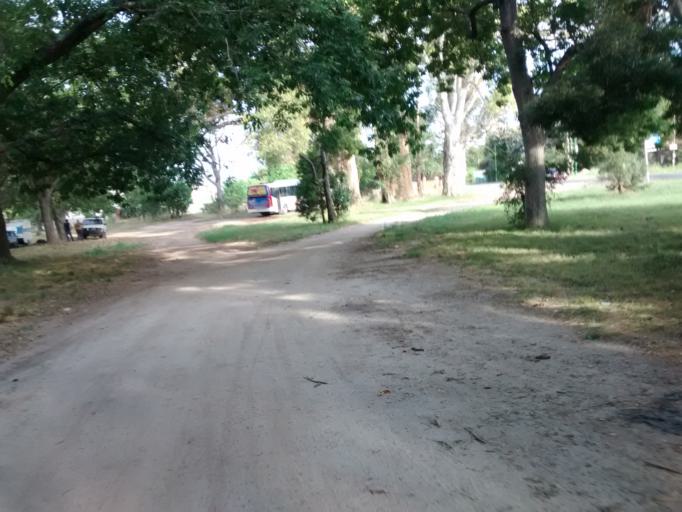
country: AR
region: Buenos Aires
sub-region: Partido de La Plata
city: La Plata
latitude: -34.8610
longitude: -58.1171
